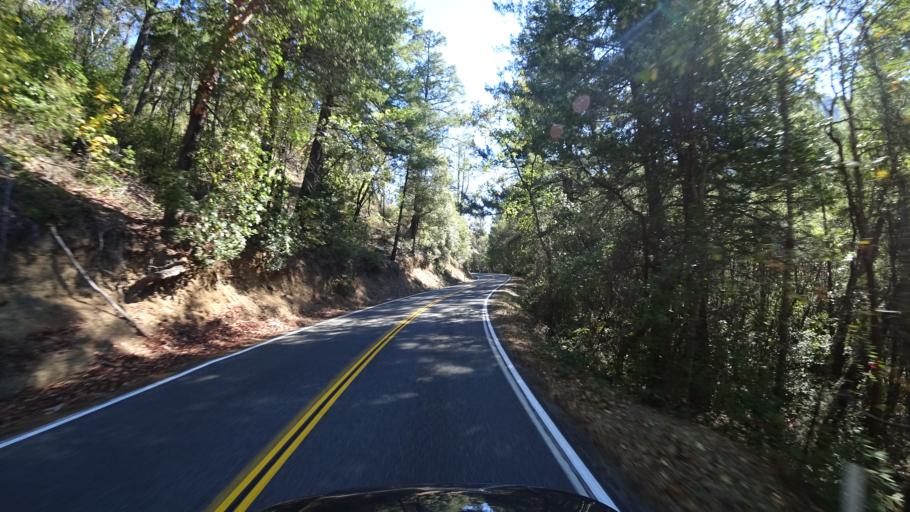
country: US
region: California
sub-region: Siskiyou County
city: Happy Camp
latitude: 41.3764
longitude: -123.4540
